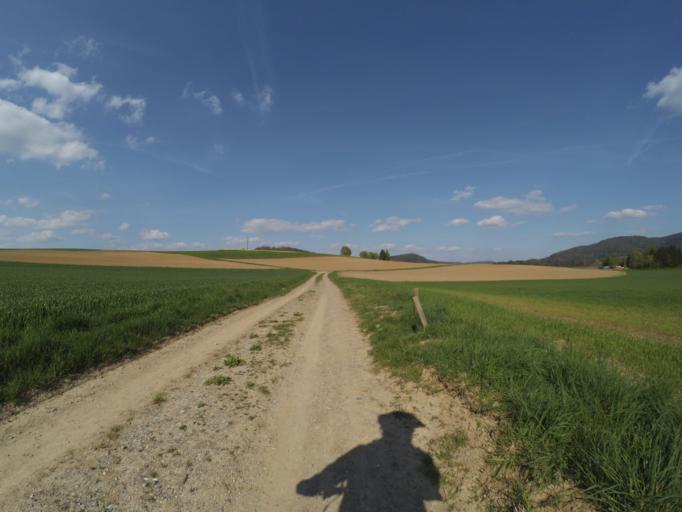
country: CH
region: Thurgau
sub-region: Frauenfeld District
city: Diessenhofen
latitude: 47.6581
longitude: 8.7596
